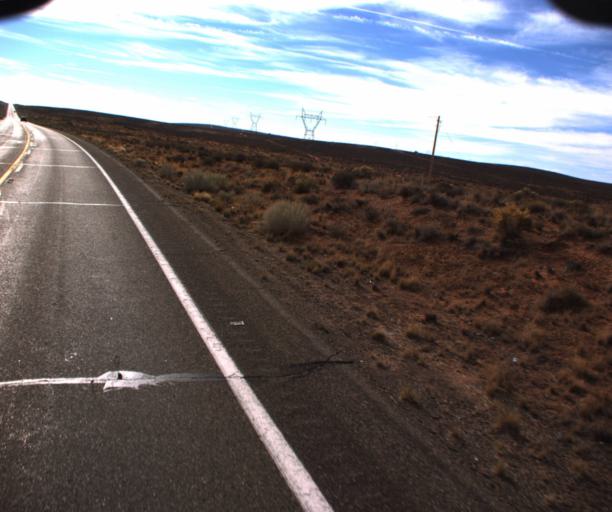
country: US
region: Arizona
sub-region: Coconino County
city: LeChee
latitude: 36.8432
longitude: -111.3283
